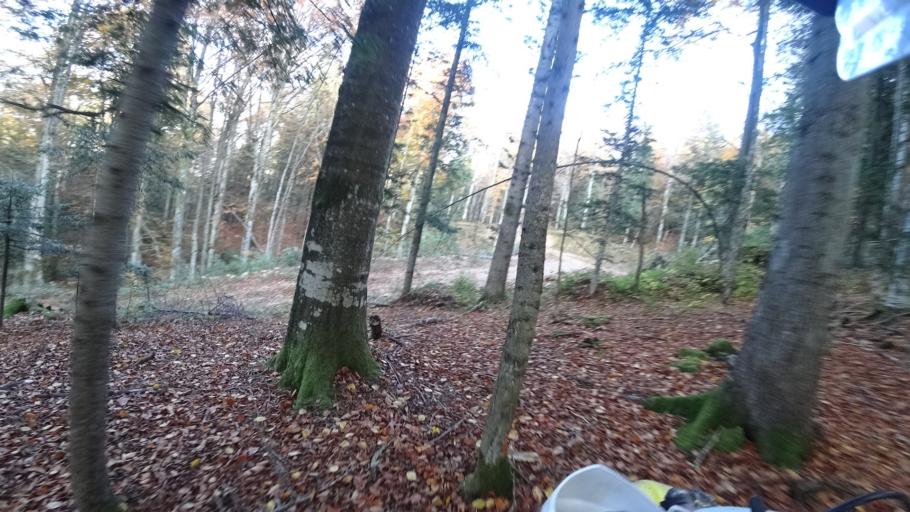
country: HR
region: Karlovacka
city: Plaski
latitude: 44.9659
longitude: 15.3897
